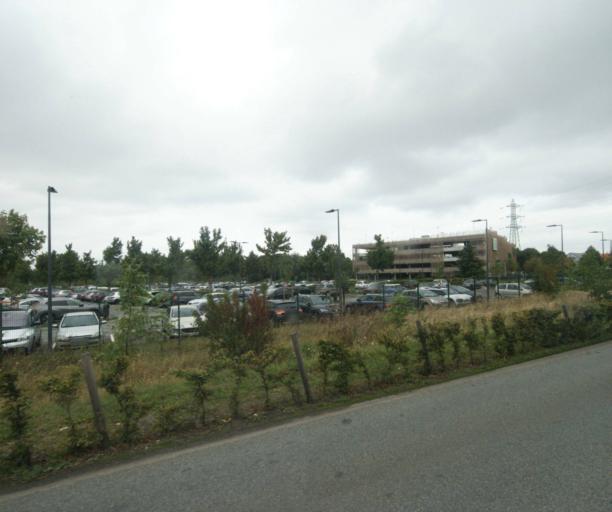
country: FR
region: Nord-Pas-de-Calais
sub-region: Departement du Nord
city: Lezennes
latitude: 50.6111
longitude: 3.1215
